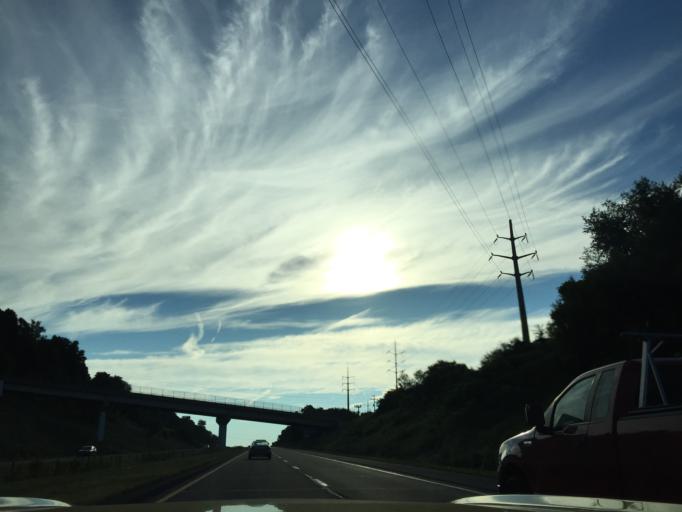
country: US
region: Pennsylvania
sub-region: Lehigh County
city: Fountain Hill
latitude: 40.5875
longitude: -75.3793
